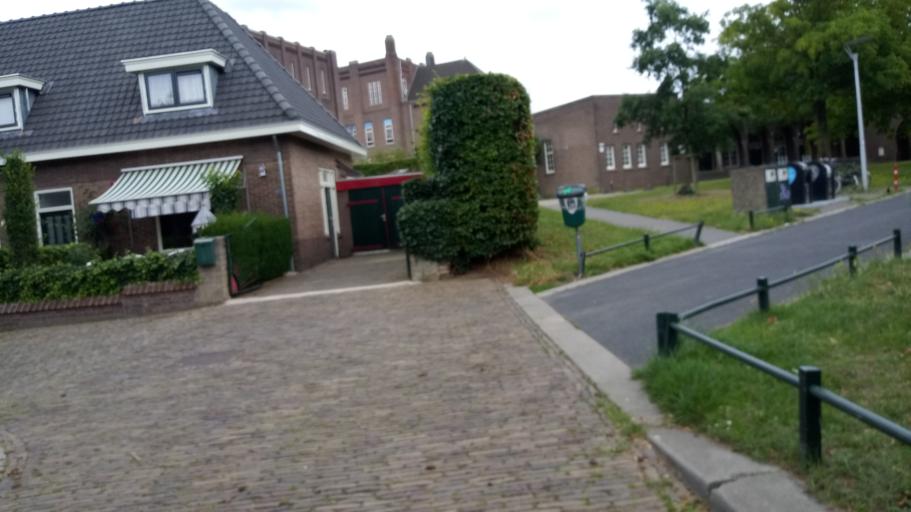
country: NL
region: Gelderland
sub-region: Gemeente Nijmegen
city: Nijmegen
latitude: 51.8336
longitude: 5.8782
